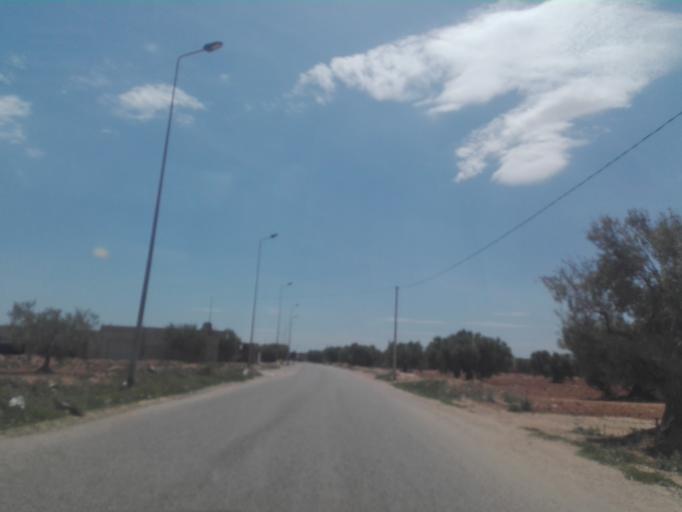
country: TN
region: Safaqis
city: Sfax
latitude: 34.6272
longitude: 10.6005
